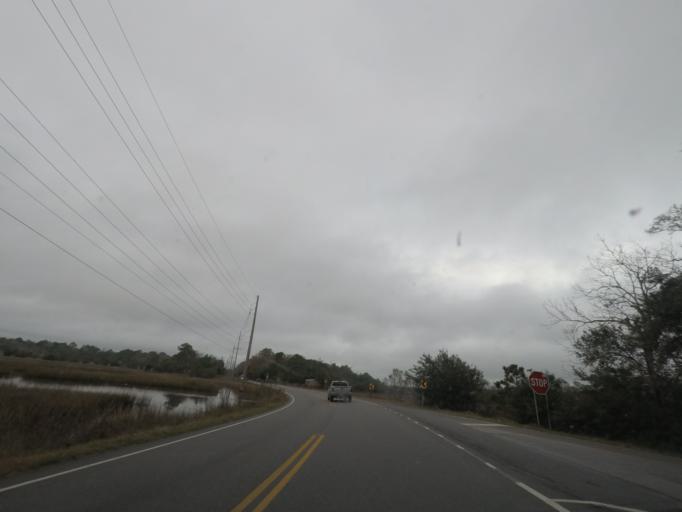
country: US
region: South Carolina
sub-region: Charleston County
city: Meggett
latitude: 32.6611
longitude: -80.3404
